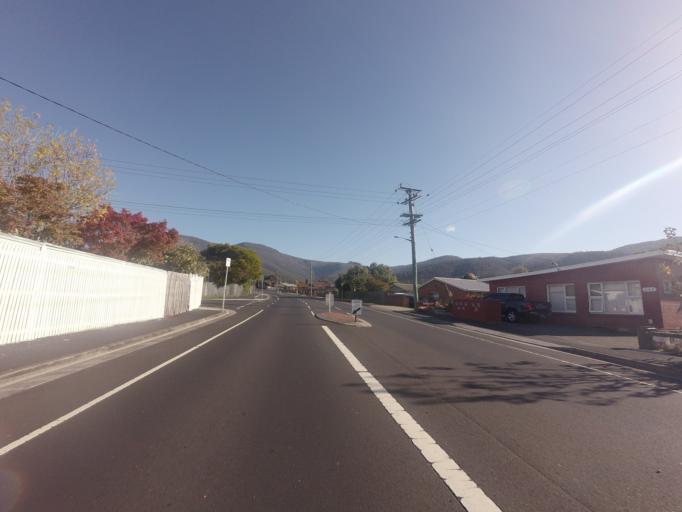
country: AU
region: Tasmania
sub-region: Glenorchy
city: Glenorchy
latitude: -42.8435
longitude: 147.2670
